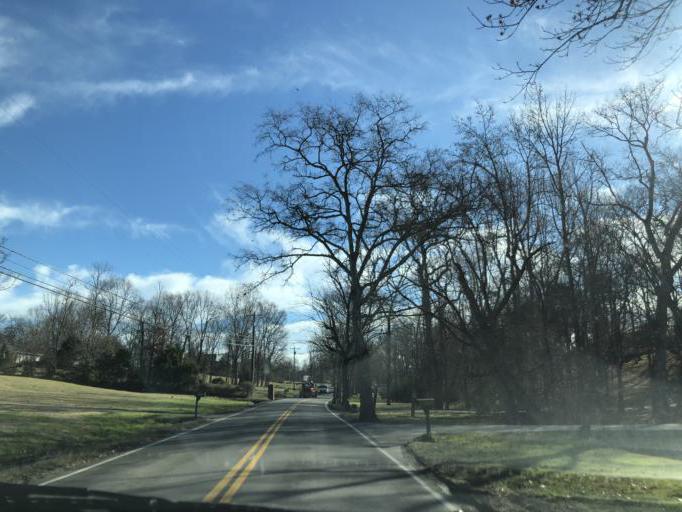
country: US
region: Tennessee
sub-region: Wilson County
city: Mount Juliet
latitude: 36.1701
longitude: -86.5591
